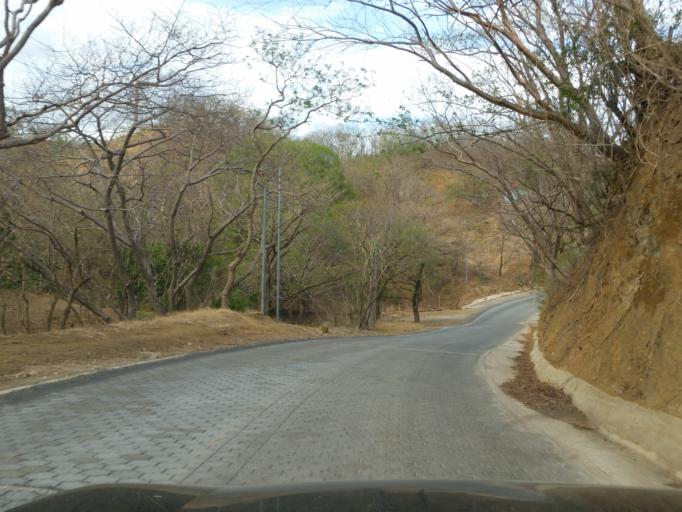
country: NI
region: Rivas
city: Tola
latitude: 11.3916
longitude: -85.9804
